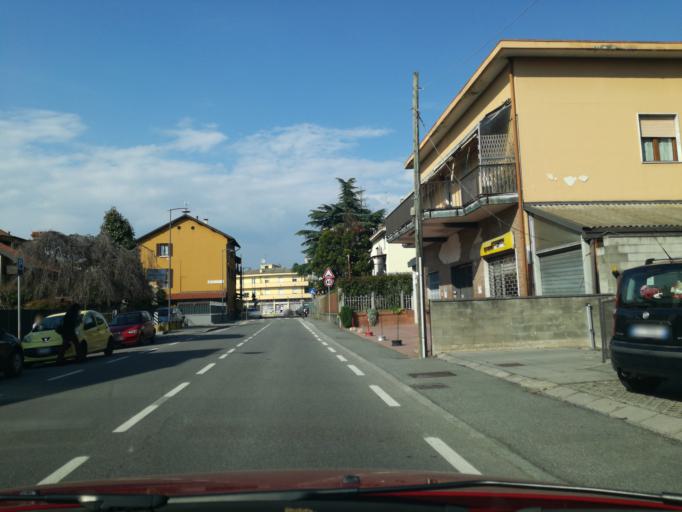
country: IT
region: Lombardy
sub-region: Provincia di Monza e Brianza
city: Cornate d'Adda
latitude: 45.6292
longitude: 9.4696
